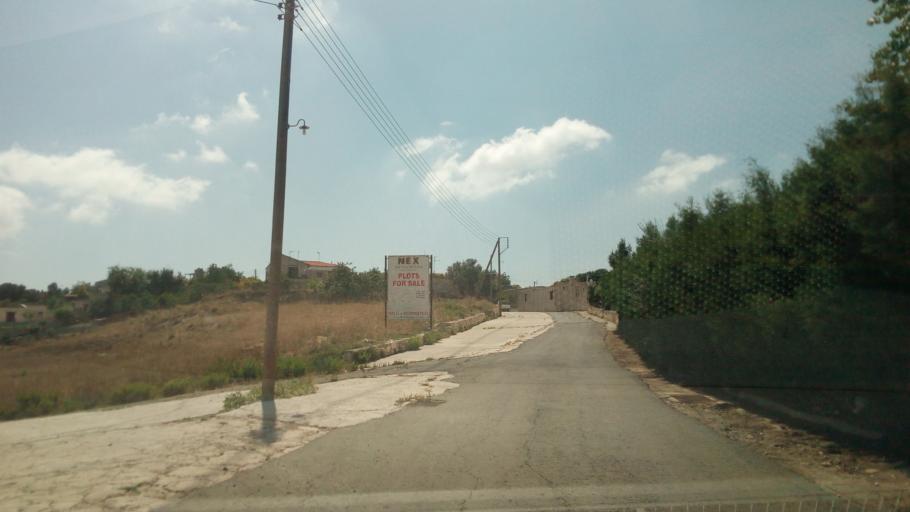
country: CY
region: Pafos
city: Tala
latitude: 34.9254
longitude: 32.5254
